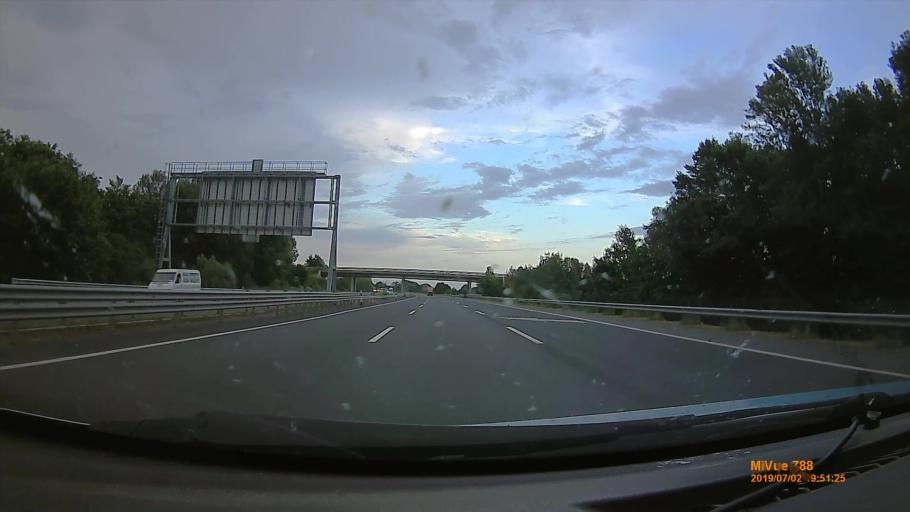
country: HU
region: Zala
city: Letenye
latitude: 46.4156
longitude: 16.7507
